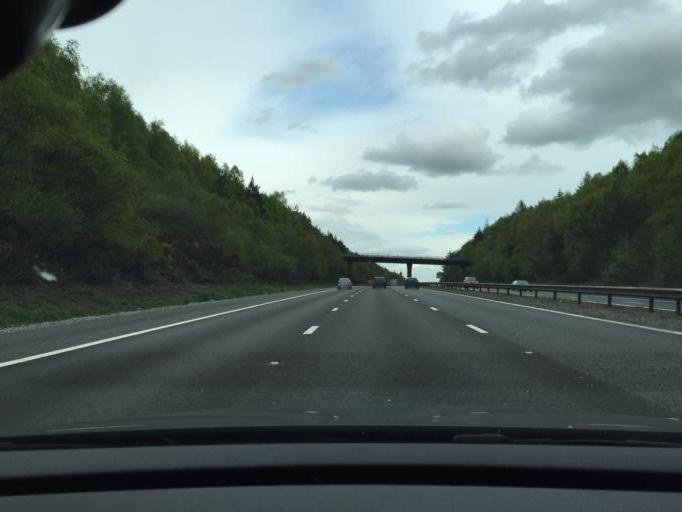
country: GB
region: England
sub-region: West Berkshire
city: Basildon
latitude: 51.4603
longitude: -1.1802
